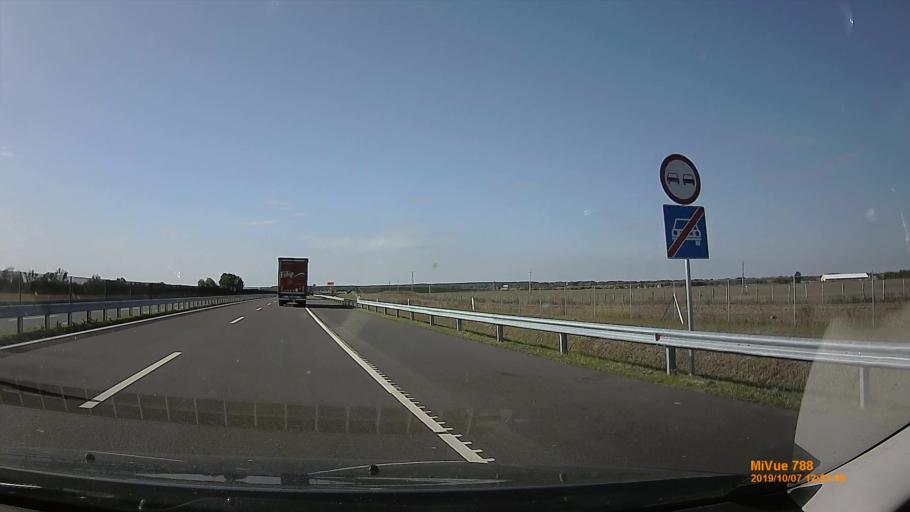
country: HU
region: Jasz-Nagykun-Szolnok
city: Cserkeszolo
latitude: 46.8805
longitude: 20.1502
